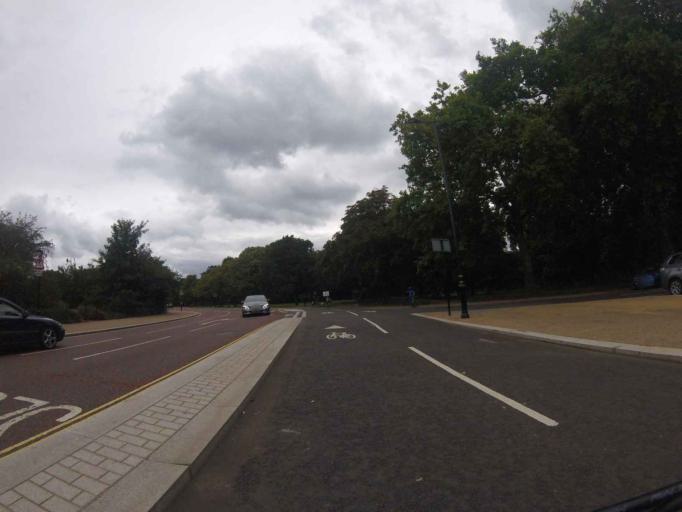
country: GB
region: England
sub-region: Greater London
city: Bayswater
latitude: 51.5071
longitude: -0.1705
